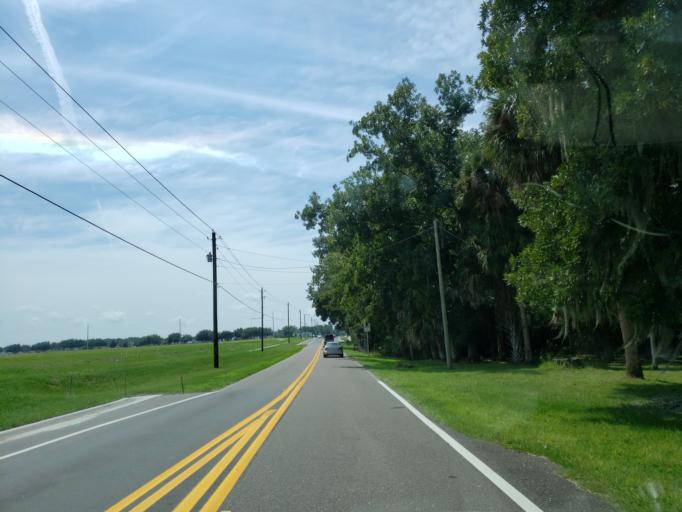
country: US
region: Florida
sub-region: Hillsborough County
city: Riverview
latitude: 27.8394
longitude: -82.3433
